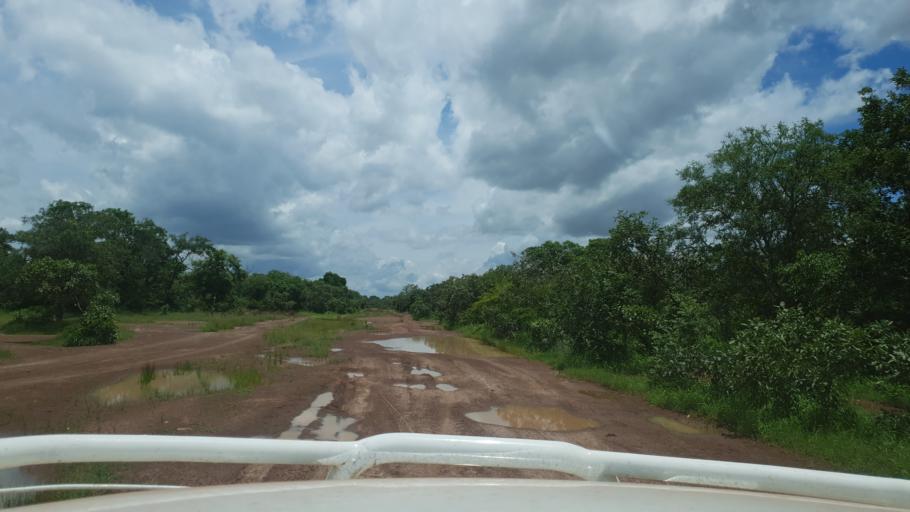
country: ML
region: Koulikoro
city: Banamba
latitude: 13.1983
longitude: -7.3279
